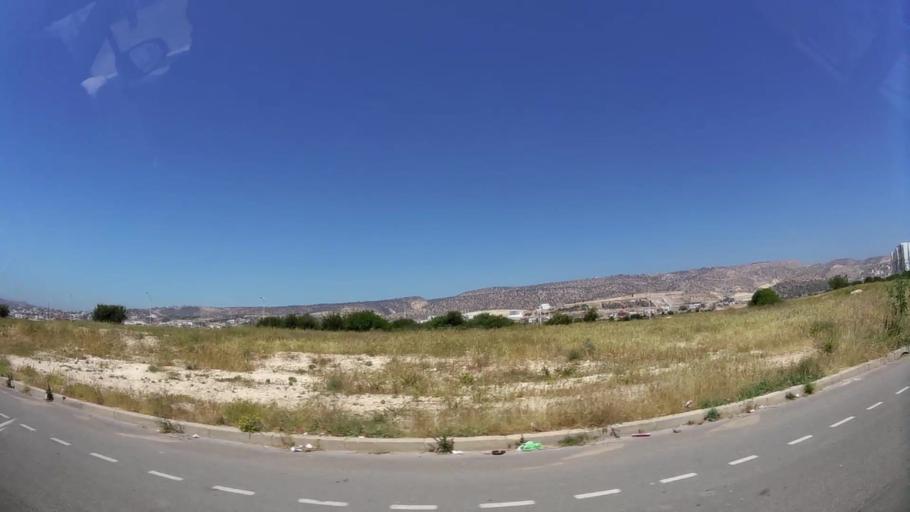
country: MA
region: Oued ed Dahab-Lagouira
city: Dakhla
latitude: 30.4377
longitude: -9.5682
